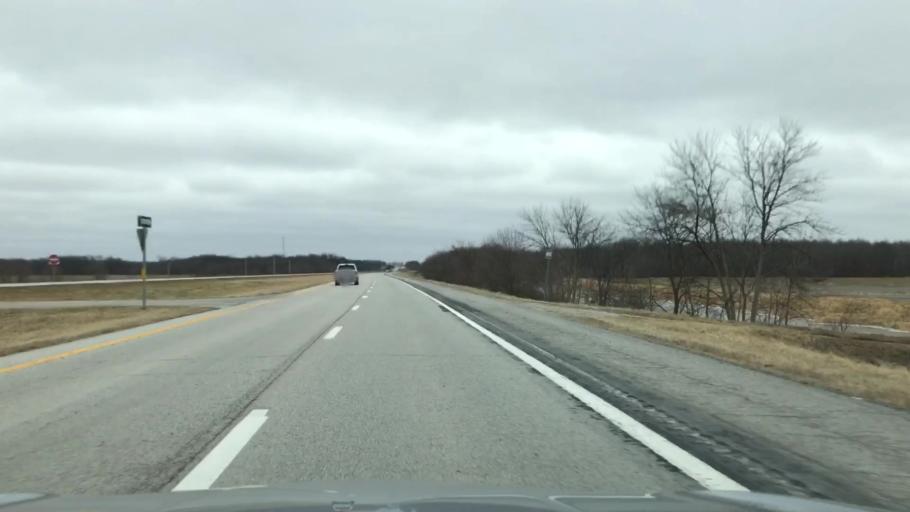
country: US
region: Missouri
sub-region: Linn County
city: Linneus
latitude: 39.7774
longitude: -93.3351
